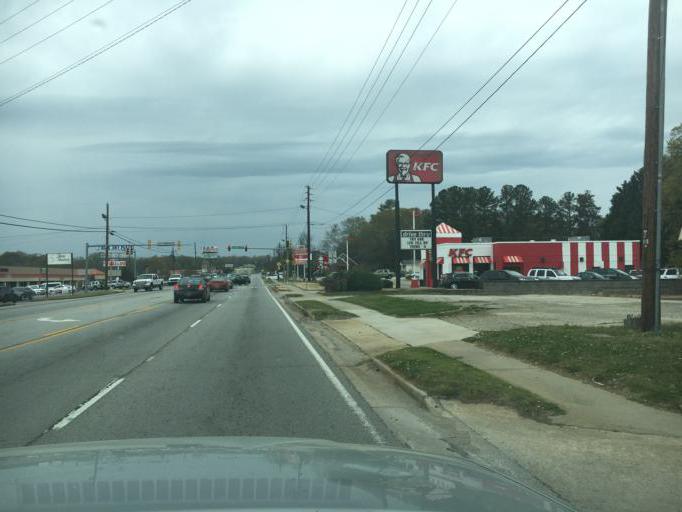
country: US
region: Georgia
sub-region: Stephens County
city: Toccoa
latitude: 34.5726
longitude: -83.3106
